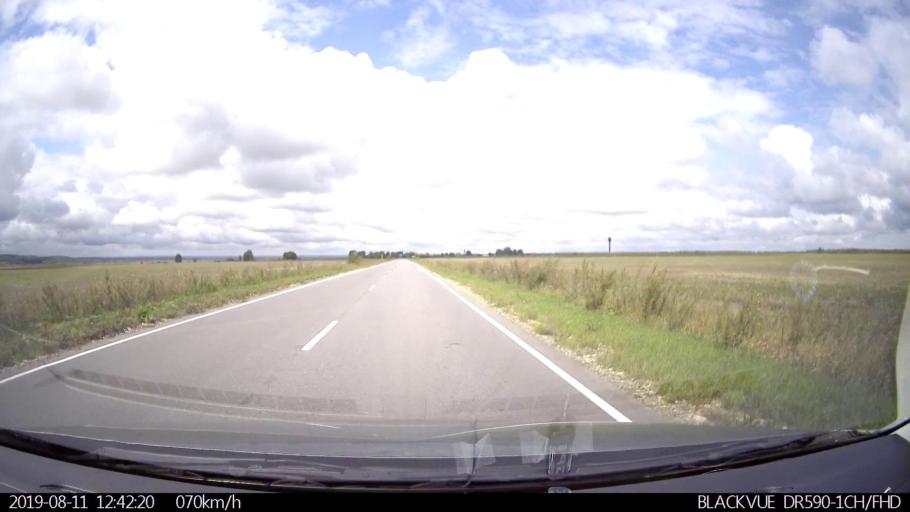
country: RU
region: Ulyanovsk
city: Ignatovka
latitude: 53.8451
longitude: 47.7527
